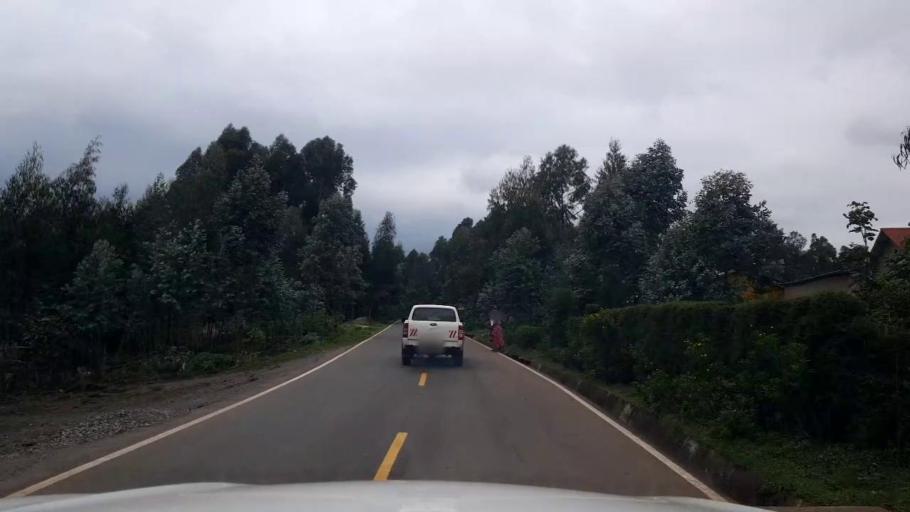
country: RW
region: Northern Province
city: Musanze
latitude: -1.4366
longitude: 29.5535
